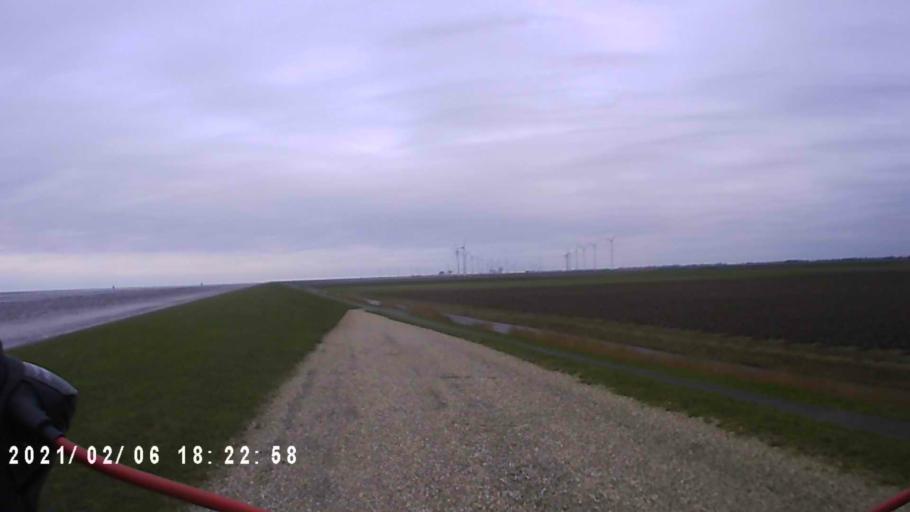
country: DE
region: Lower Saxony
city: Borkum
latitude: 53.4635
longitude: 6.7177
